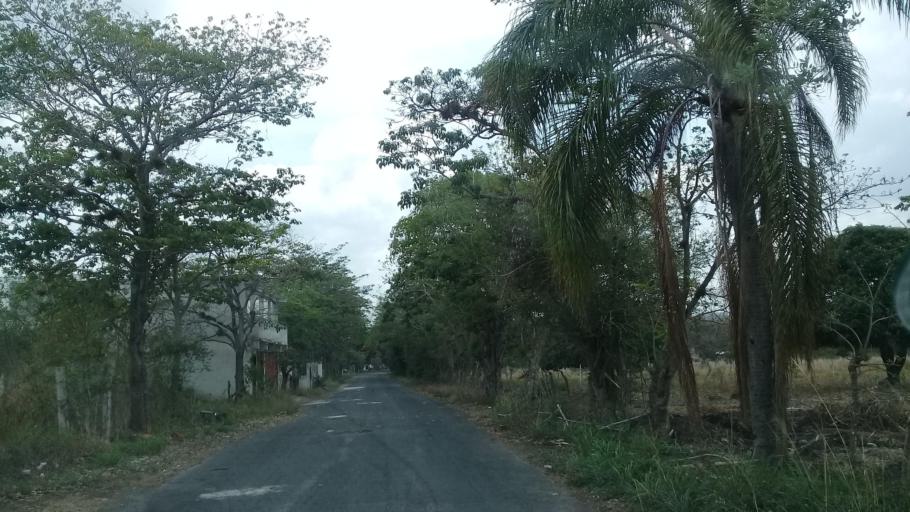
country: MX
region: Veracruz
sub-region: Emiliano Zapata
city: Plan del Rio
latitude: 19.4286
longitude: -96.6940
